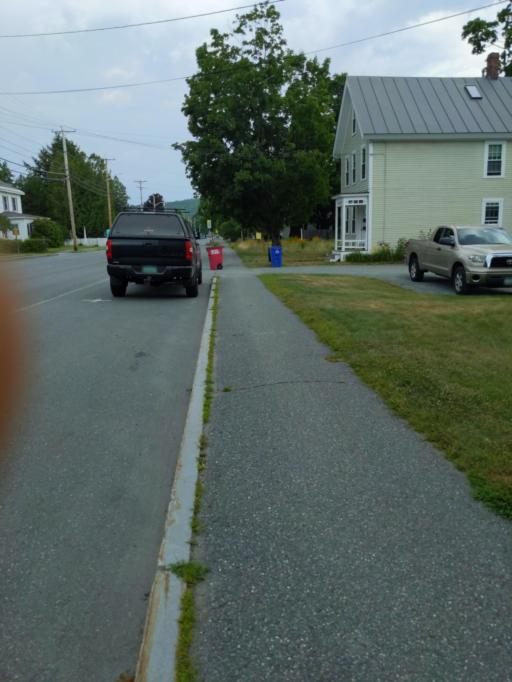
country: US
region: New Hampshire
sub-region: Grafton County
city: Lebanon
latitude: 43.6390
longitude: -72.2482
